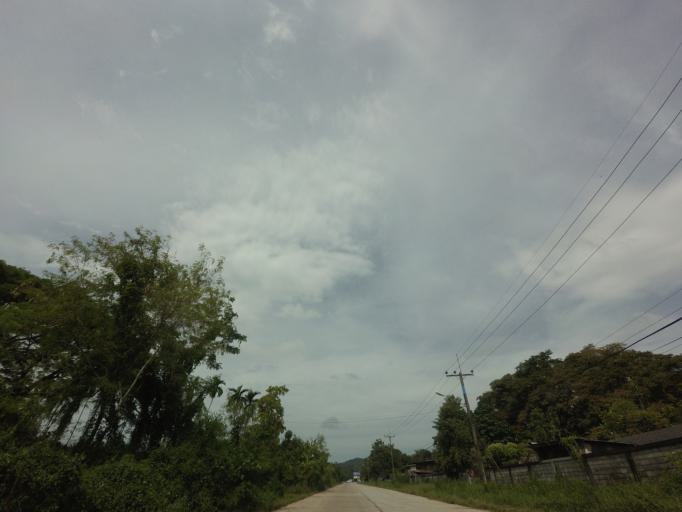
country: TH
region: Rayong
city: Klaeng
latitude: 12.6872
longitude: 101.5380
